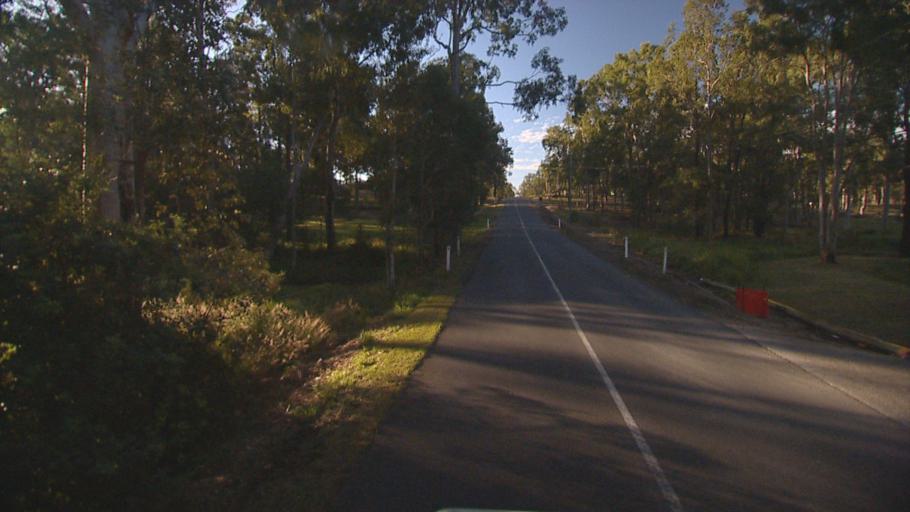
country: AU
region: Queensland
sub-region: Logan
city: Waterford West
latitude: -27.7342
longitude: 153.1456
